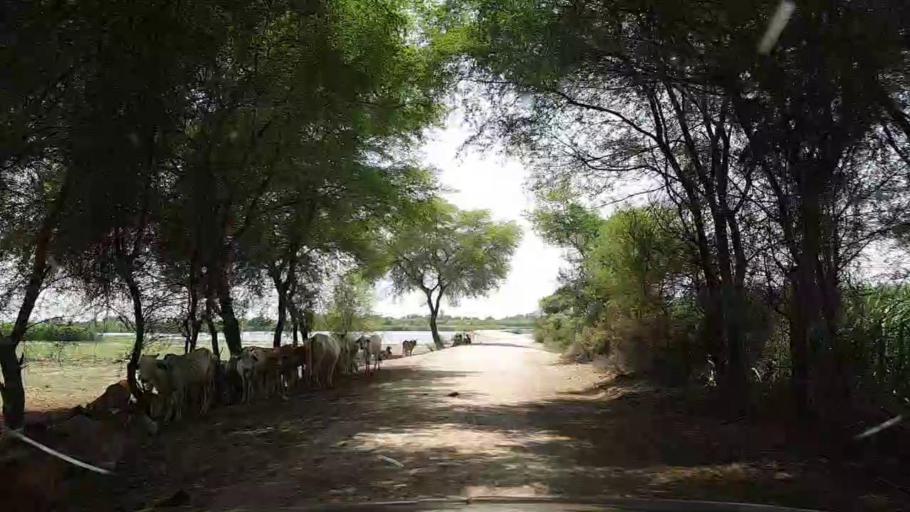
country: PK
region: Sindh
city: Ghotki
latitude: 28.0817
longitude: 69.3125
